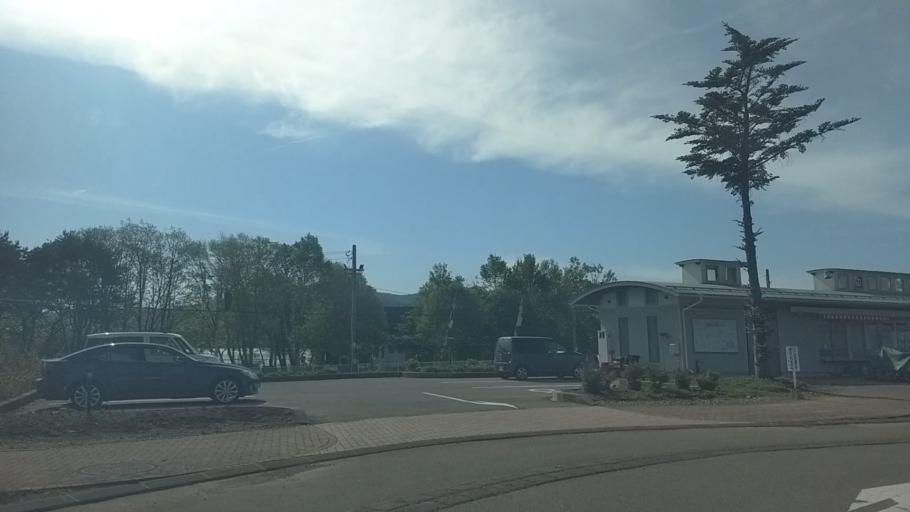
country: JP
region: Yamanashi
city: Nirasaki
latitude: 35.9559
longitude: 138.4742
